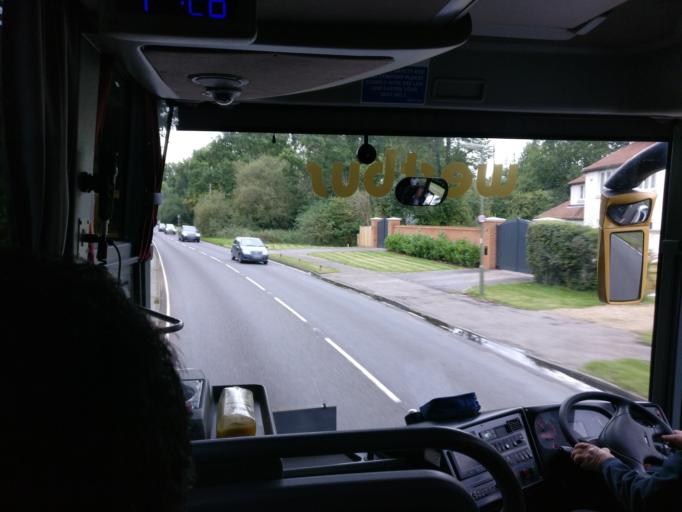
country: GB
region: England
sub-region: Surrey
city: Chobham
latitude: 51.3444
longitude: -0.5988
